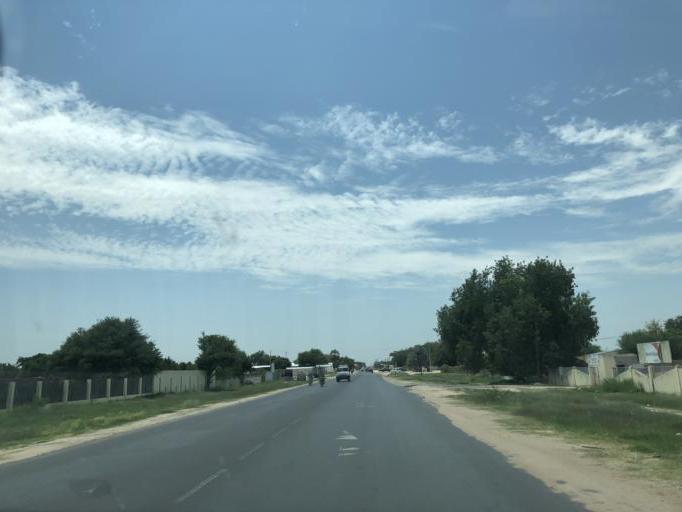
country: AO
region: Cunene
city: Ondjiva
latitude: -17.0907
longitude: 15.7450
